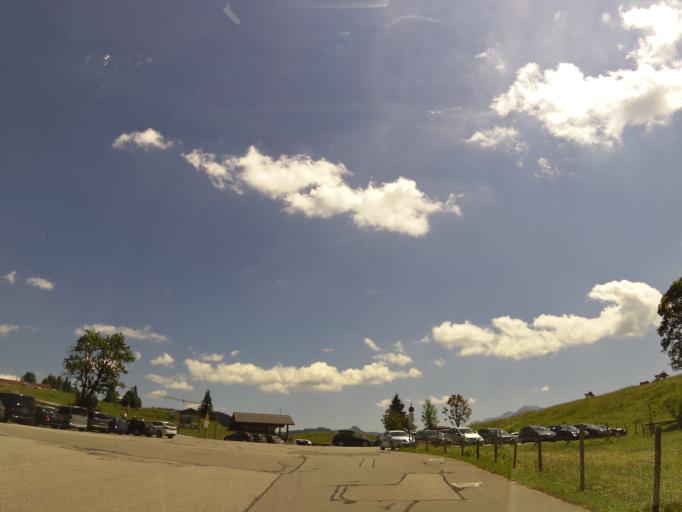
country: AT
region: Tyrol
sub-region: Politischer Bezirk Kitzbuhel
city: Waidring
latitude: 47.6580
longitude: 12.5787
